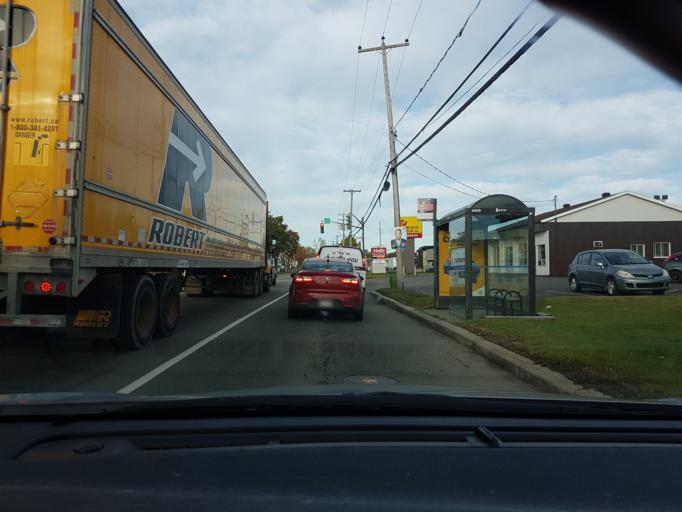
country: CA
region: Quebec
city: L'Ancienne-Lorette
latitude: 46.8065
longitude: -71.2980
